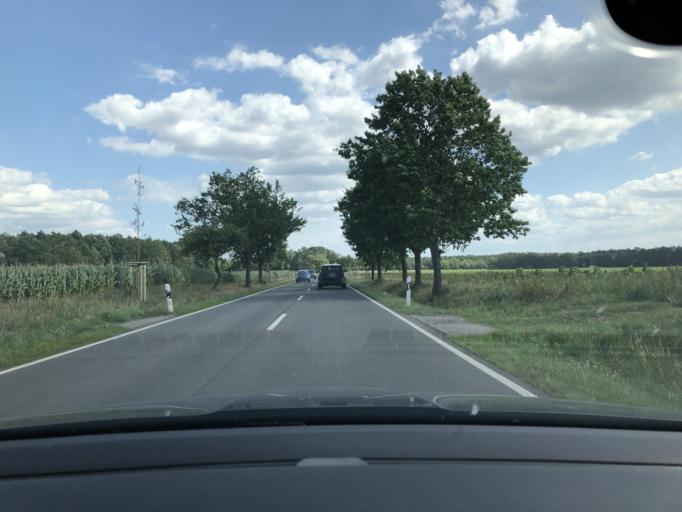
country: DE
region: Brandenburg
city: Wittstock
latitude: 53.0748
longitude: 12.4958
